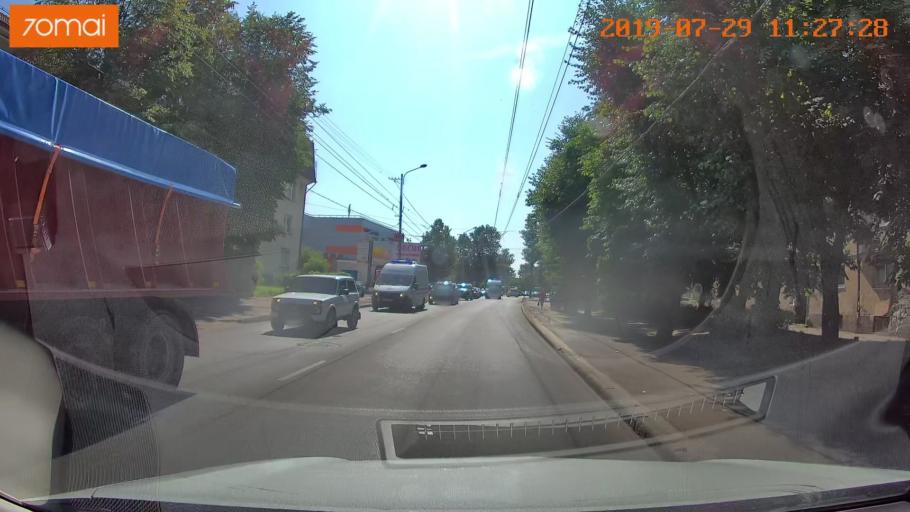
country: RU
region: Kaliningrad
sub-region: Gorod Kaliningrad
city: Kaliningrad
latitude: 54.6911
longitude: 20.5296
